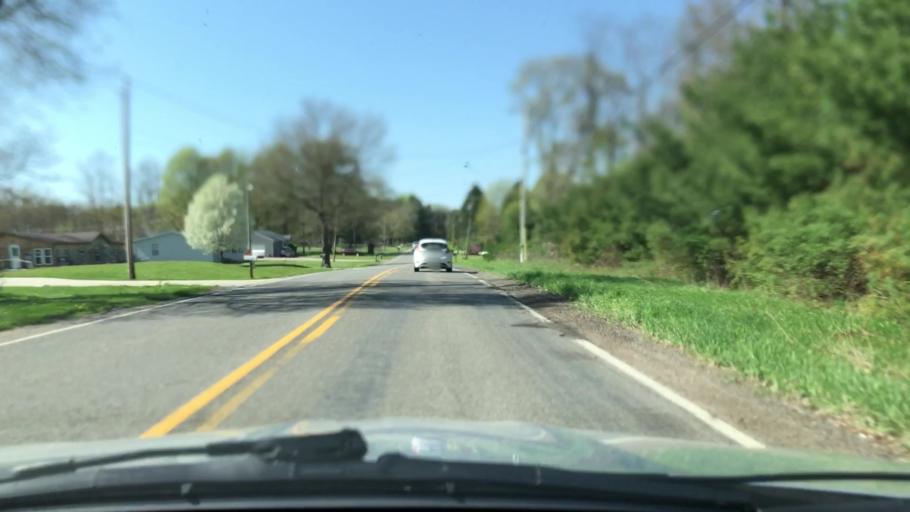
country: US
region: Indiana
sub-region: Saint Joseph County
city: Georgetown
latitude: 41.7540
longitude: -86.3021
